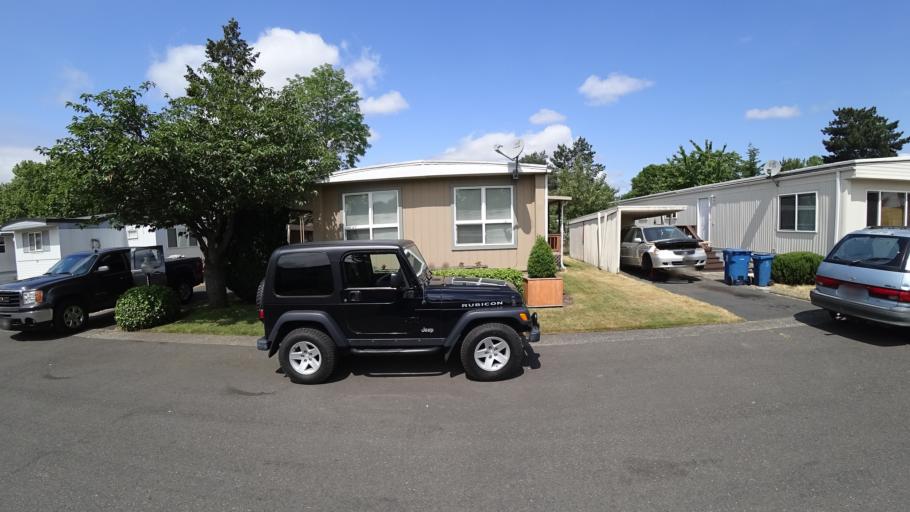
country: US
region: Washington
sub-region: Clark County
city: Vancouver
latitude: 45.6166
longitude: -122.6841
